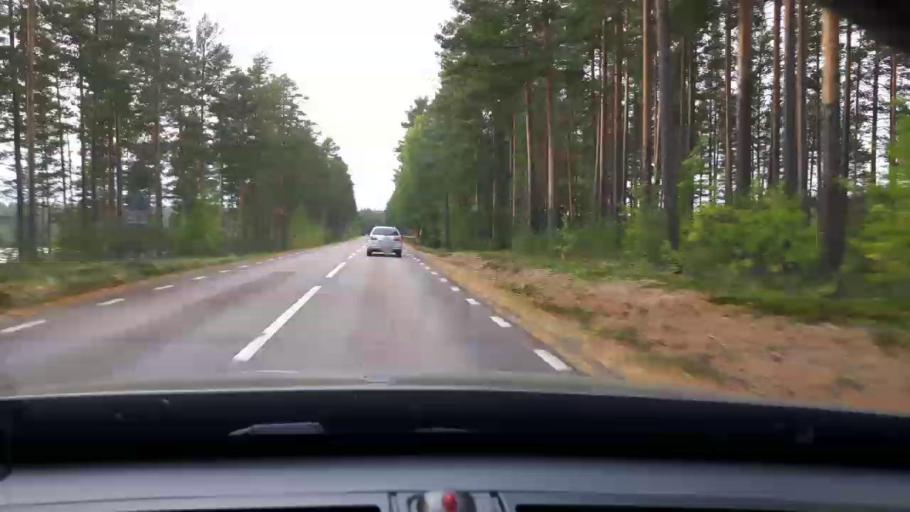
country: SE
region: Dalarna
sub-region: Gagnefs Kommun
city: Mockfjard
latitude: 60.3531
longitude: 14.8597
